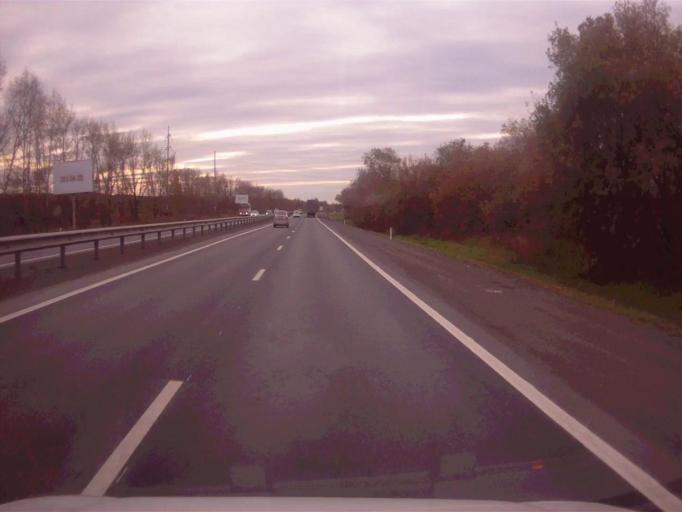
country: RU
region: Chelyabinsk
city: Roza
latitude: 54.9860
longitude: 61.4344
